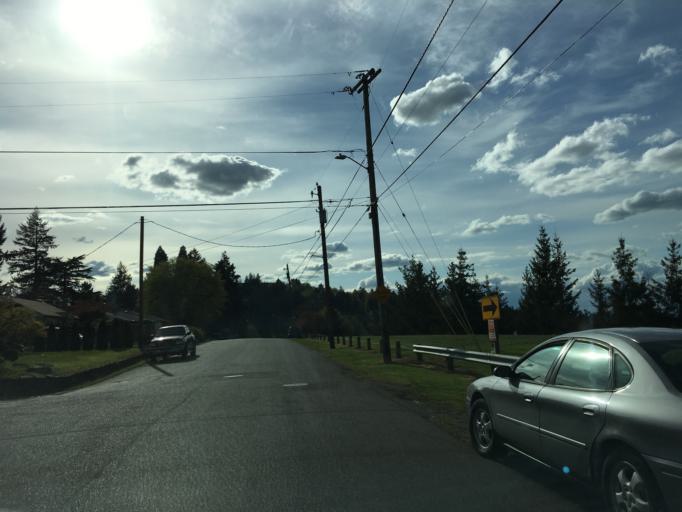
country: US
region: Oregon
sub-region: Multnomah County
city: Lents
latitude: 45.5468
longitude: -122.5512
